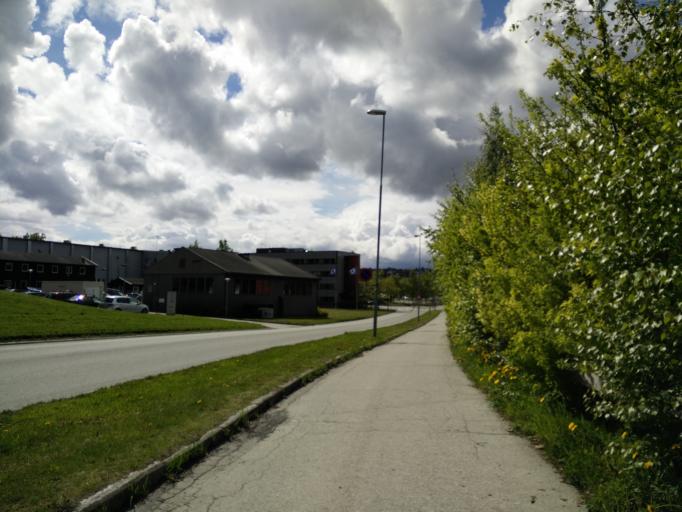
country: NO
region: Sor-Trondelag
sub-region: Trondheim
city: Trondheim
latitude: 63.4097
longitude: 10.4061
